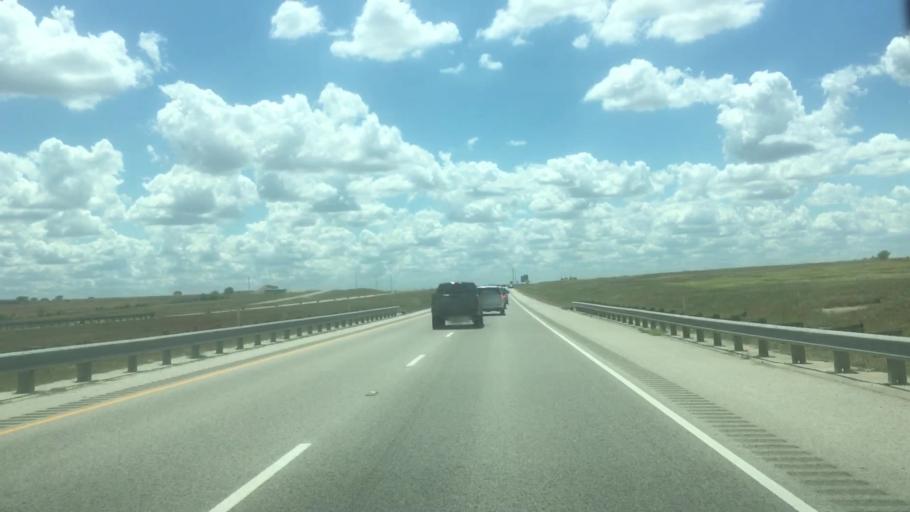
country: US
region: Texas
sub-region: Caldwell County
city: Martindale
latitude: 29.7938
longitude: -97.7826
